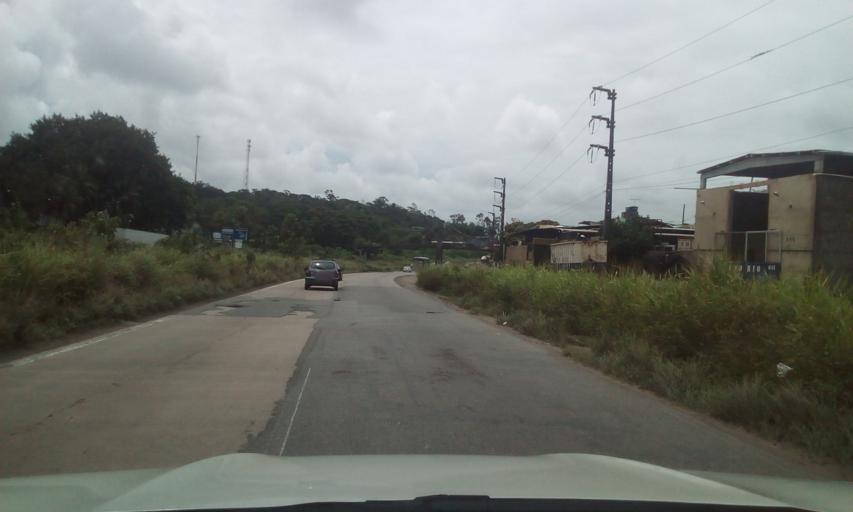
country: BR
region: Pernambuco
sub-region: Abreu E Lima
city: Abreu e Lima
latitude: -7.9350
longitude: -34.9028
